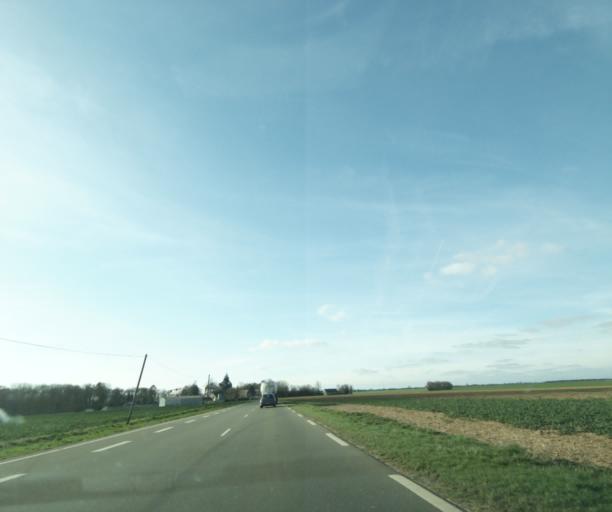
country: FR
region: Ile-de-France
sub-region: Departement des Yvelines
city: Ablis
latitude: 48.4673
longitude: 1.8726
